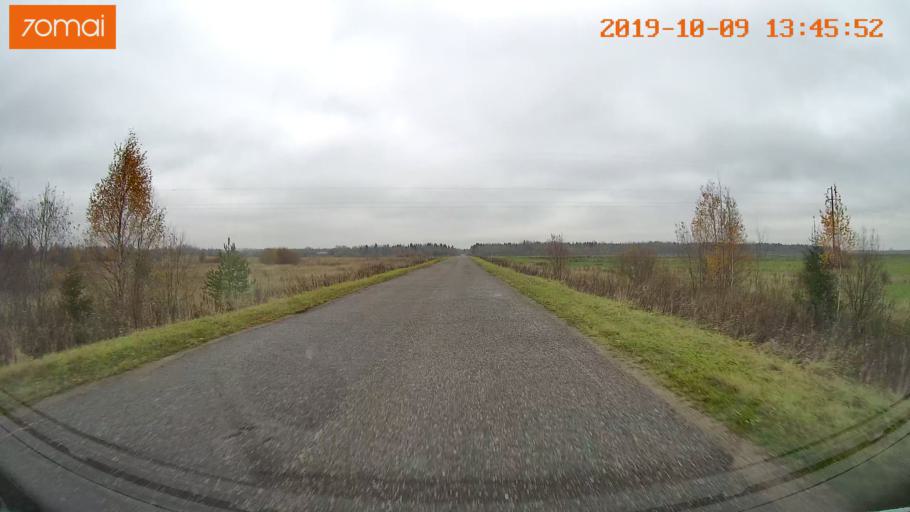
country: RU
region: Kostroma
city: Buy
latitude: 58.3783
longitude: 41.2135
